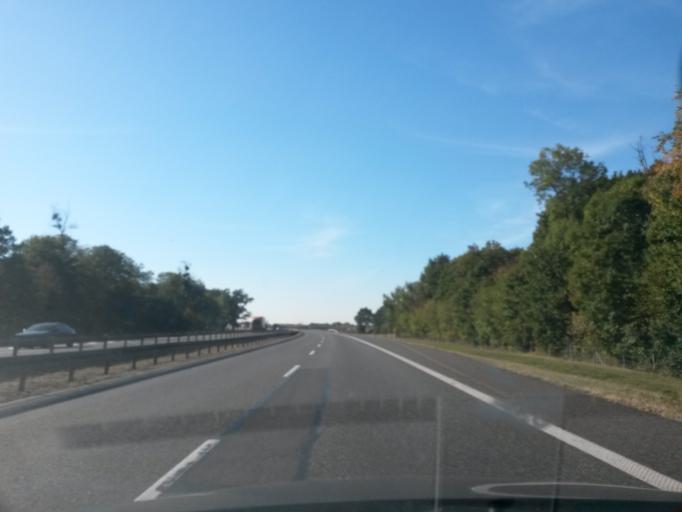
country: PL
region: Opole Voivodeship
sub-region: Powiat brzeski
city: Grodkow
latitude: 50.7682
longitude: 17.4051
